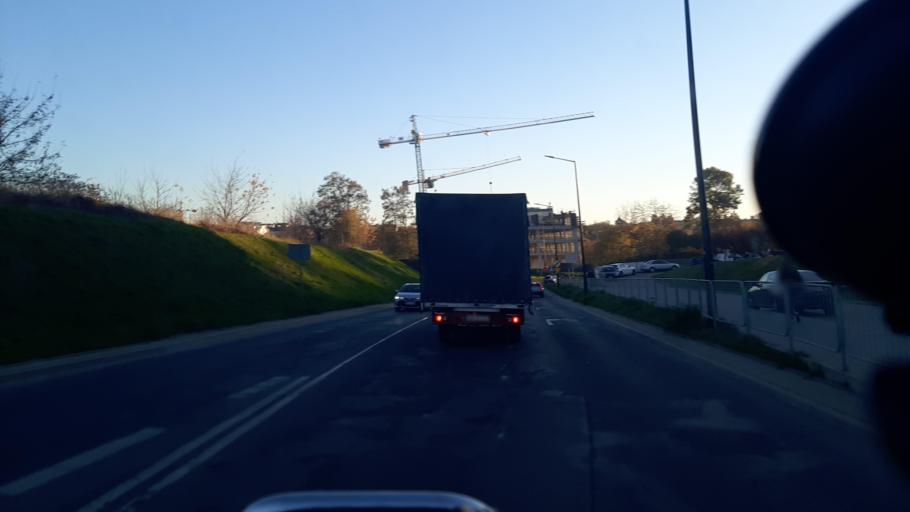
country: PL
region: Lublin Voivodeship
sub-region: Powiat lubelski
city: Lublin
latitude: 51.2561
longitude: 22.5583
